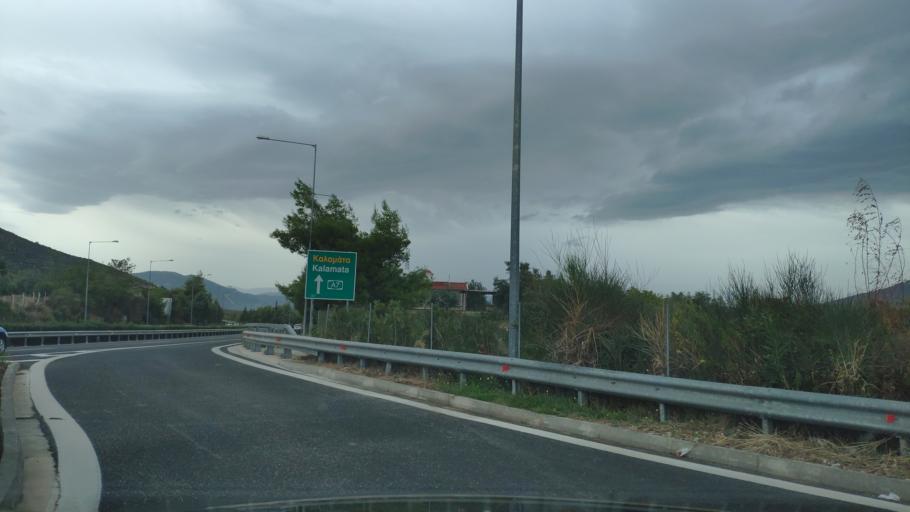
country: GR
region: Peloponnese
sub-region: Nomos Korinthias
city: Khiliomodhi
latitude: 37.8620
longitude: 22.8390
